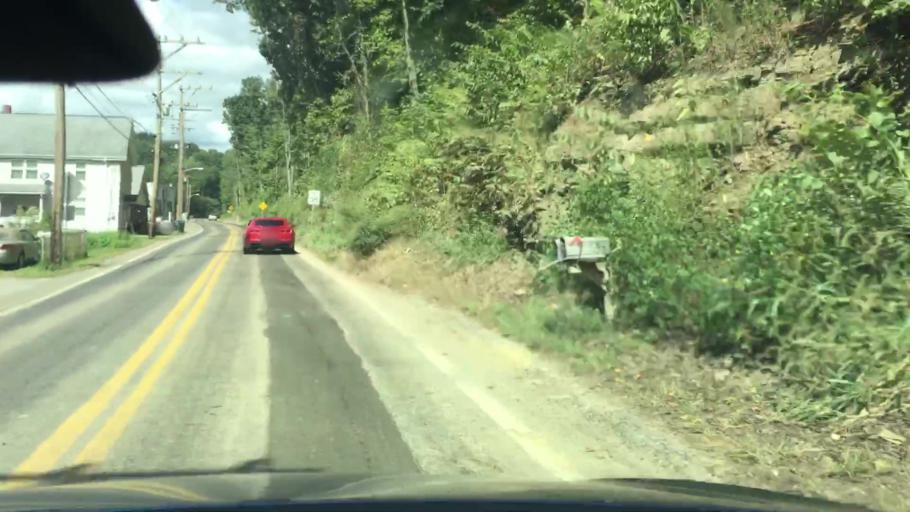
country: US
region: Pennsylvania
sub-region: Allegheny County
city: Russellton
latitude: 40.5843
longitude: -79.8272
